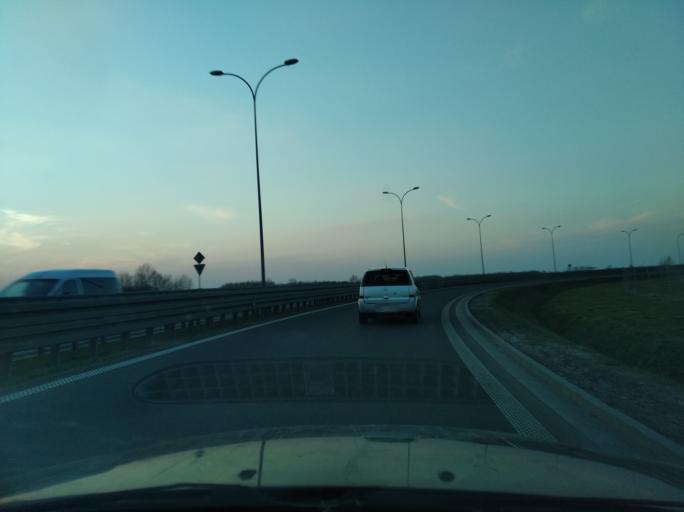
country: PL
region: Subcarpathian Voivodeship
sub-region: Powiat przeworski
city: Gorliczyna
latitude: 50.0808
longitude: 22.4743
